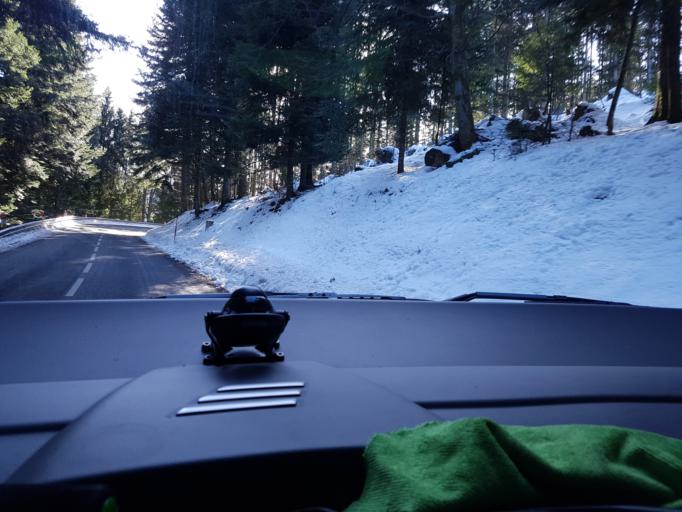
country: FR
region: Alsace
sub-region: Departement du Haut-Rhin
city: Metzeral
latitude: 47.9877
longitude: 7.0589
